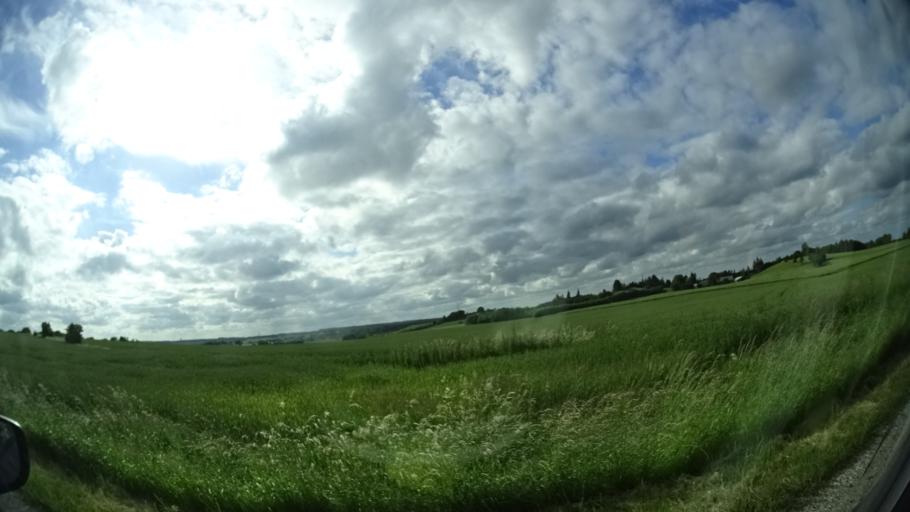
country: DK
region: Central Jutland
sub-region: Syddjurs Kommune
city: Ronde
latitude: 56.3410
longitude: 10.4483
